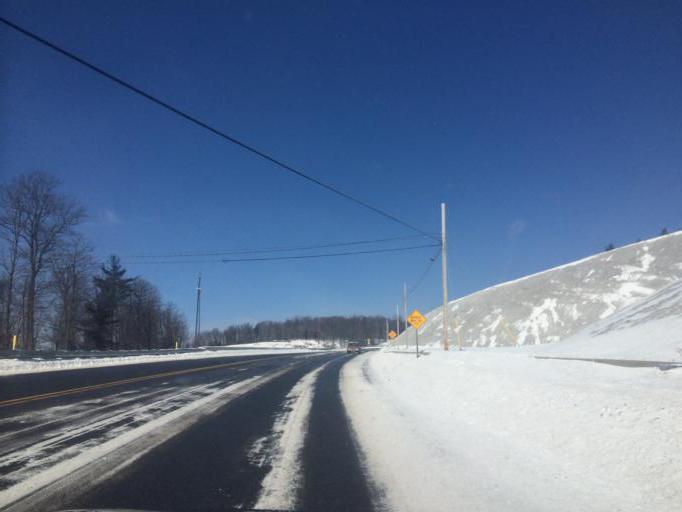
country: US
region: Pennsylvania
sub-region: Centre County
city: Park Forest Village
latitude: 40.8314
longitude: -77.9665
